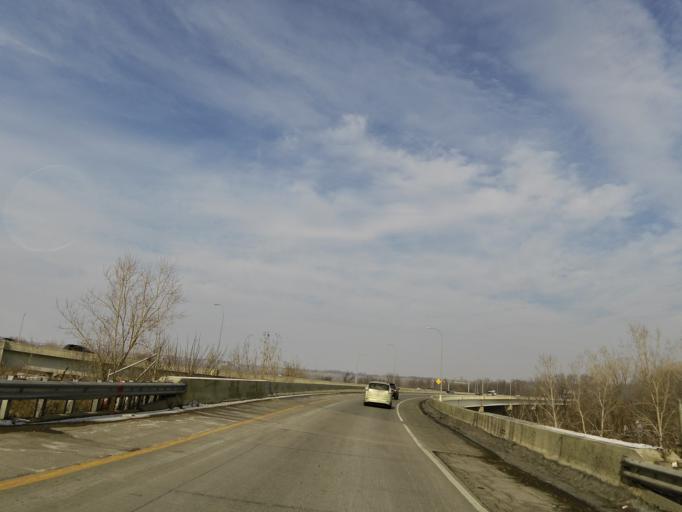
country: US
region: Minnesota
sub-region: Scott County
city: Savage
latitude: 44.7899
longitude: -93.4043
